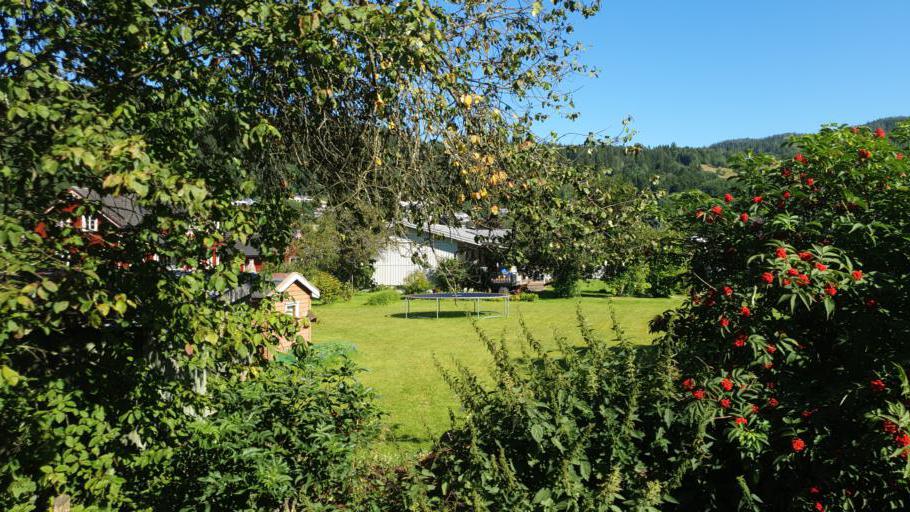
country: NO
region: Sor-Trondelag
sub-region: Orkdal
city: Orkanger
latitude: 63.2881
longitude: 9.8430
